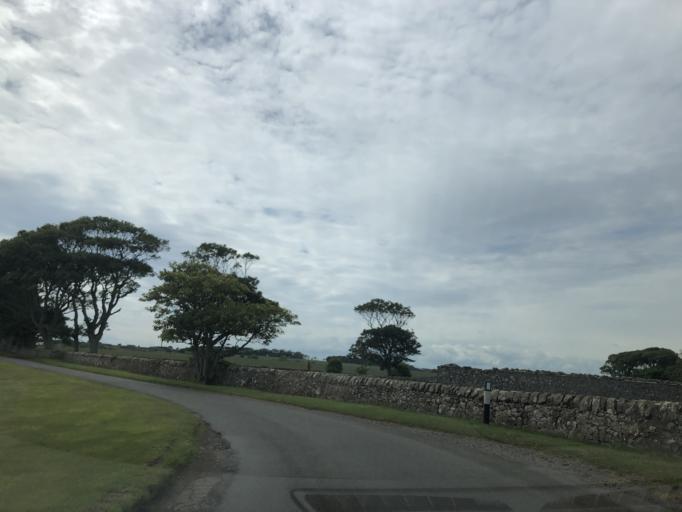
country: GB
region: Scotland
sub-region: Fife
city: Anstruther
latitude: 56.2787
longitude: -2.6039
